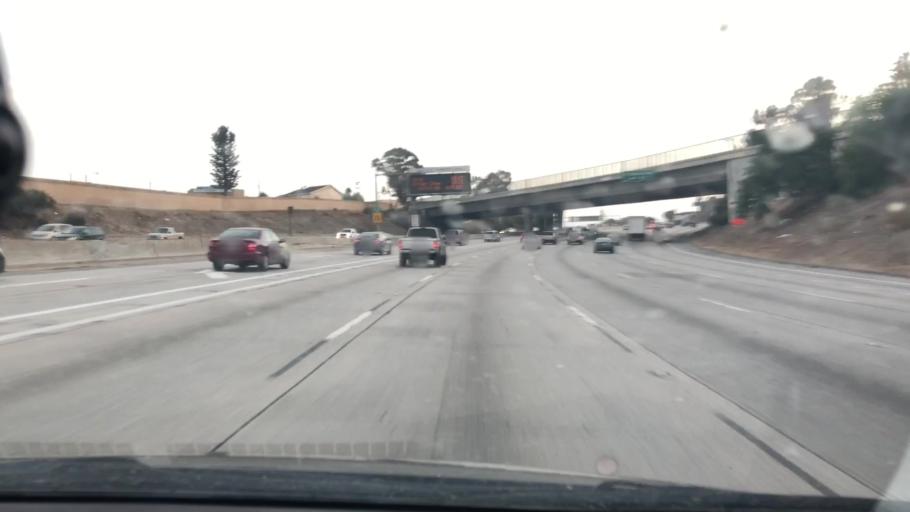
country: US
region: California
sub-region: Los Angeles County
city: West Athens
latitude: 33.9218
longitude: -118.2820
